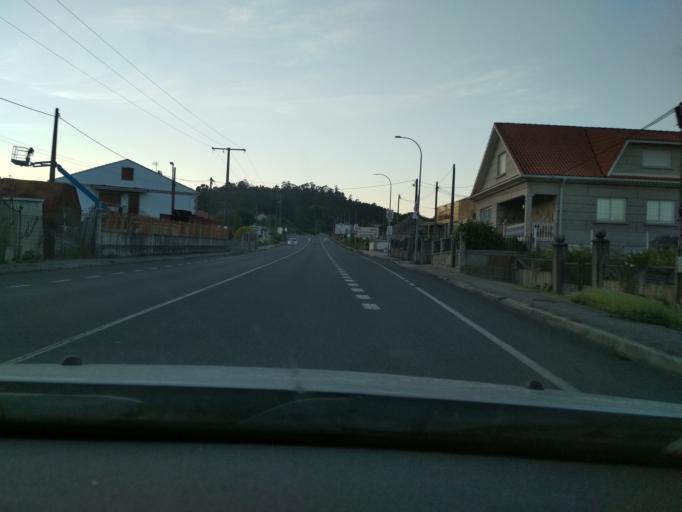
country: ES
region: Galicia
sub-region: Provincia de Pontevedra
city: Caldas de Reis
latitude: 42.6116
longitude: -8.6468
